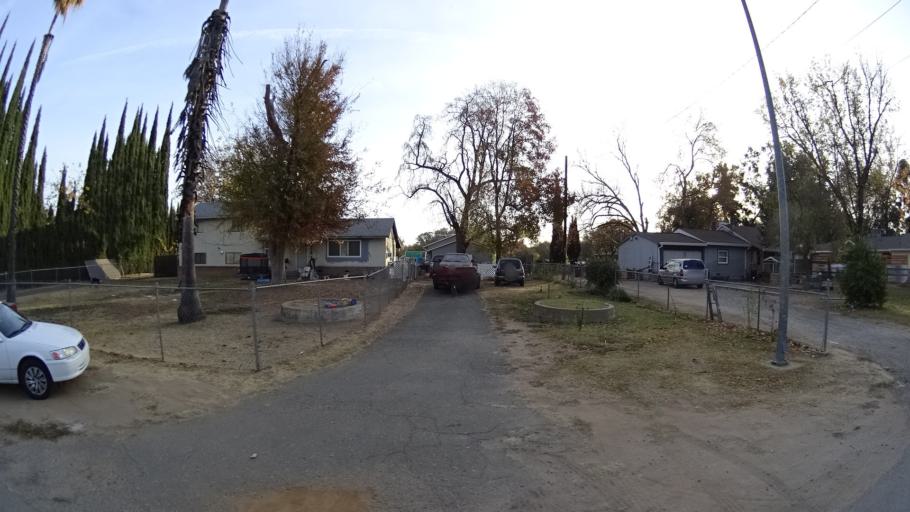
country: US
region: California
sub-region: Sacramento County
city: Citrus Heights
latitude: 38.7175
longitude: -121.2790
